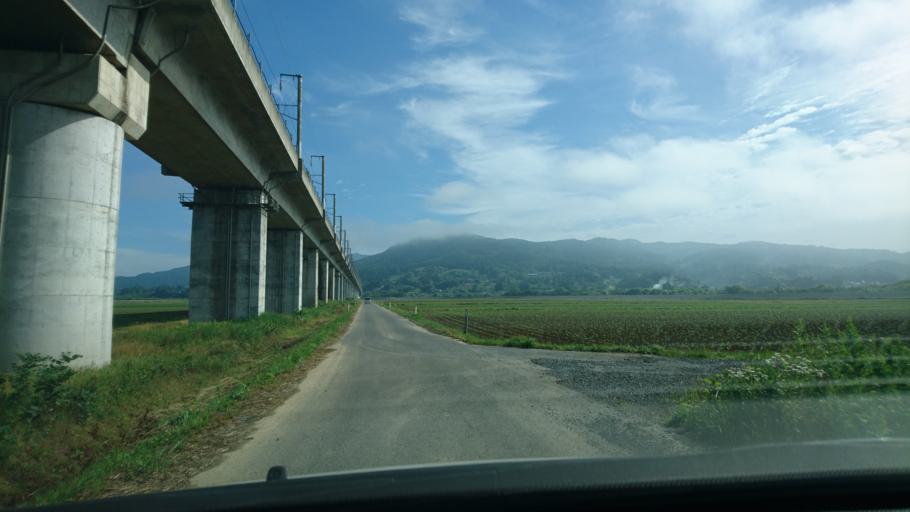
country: JP
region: Iwate
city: Ichinoseki
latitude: 38.9631
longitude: 141.1525
